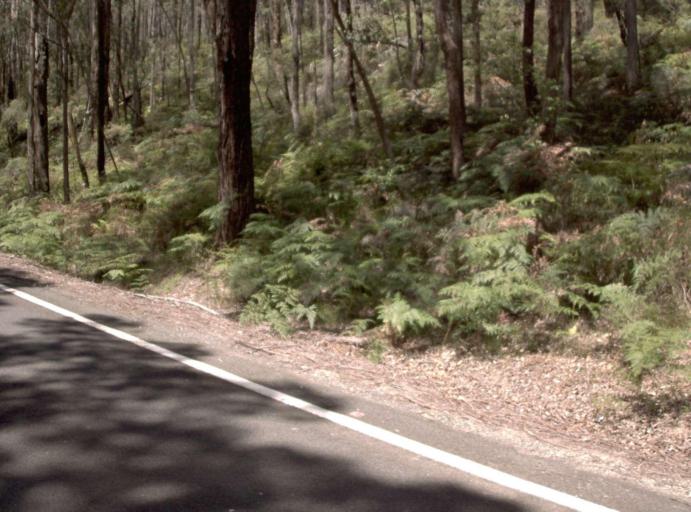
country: AU
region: New South Wales
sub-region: Bombala
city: Bombala
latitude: -37.5937
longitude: 148.9152
